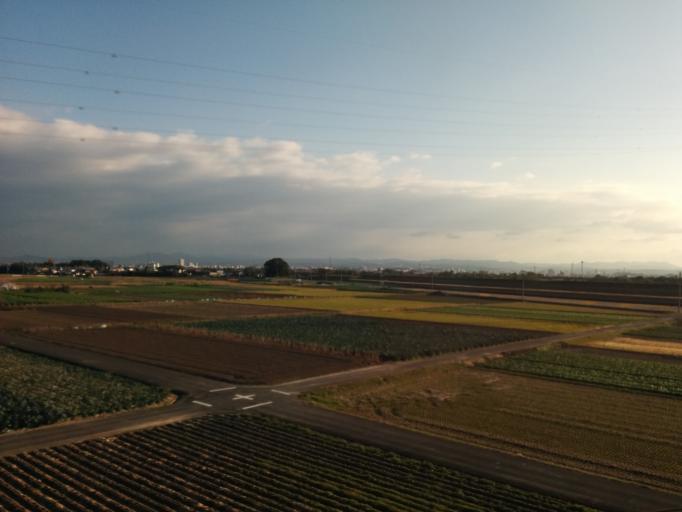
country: JP
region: Aichi
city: Anjo
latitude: 34.9202
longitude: 137.1054
